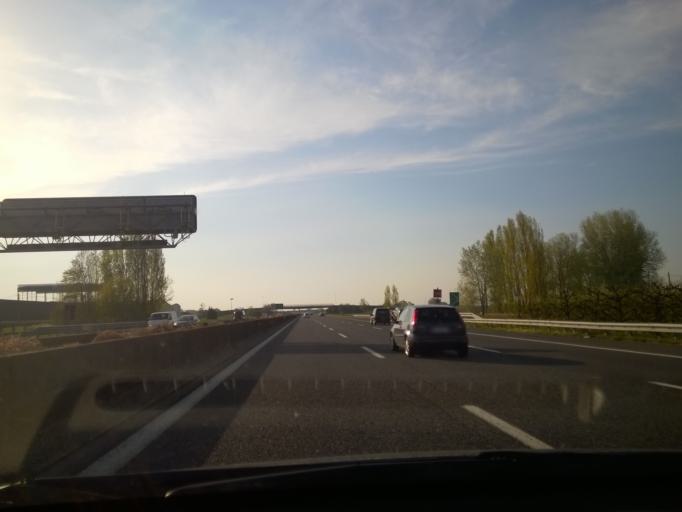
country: IT
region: Emilia-Romagna
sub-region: Provincia di Ravenna
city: Faenza
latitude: 44.3309
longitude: 11.8870
